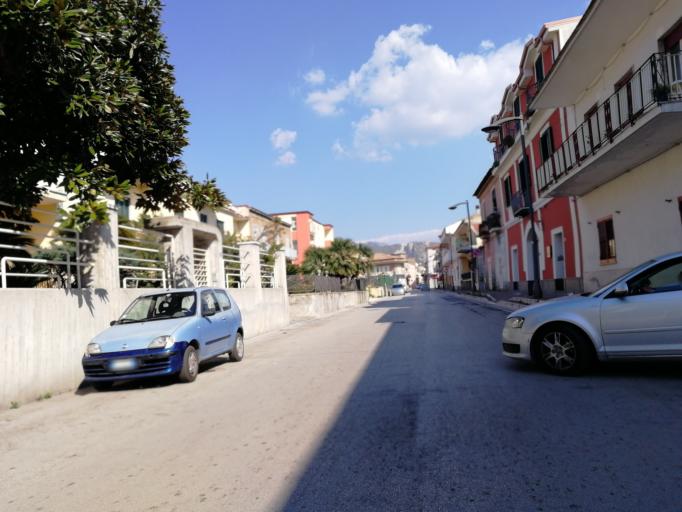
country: IT
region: Campania
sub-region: Provincia di Caserta
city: San Prisco
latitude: 41.0838
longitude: 14.2737
